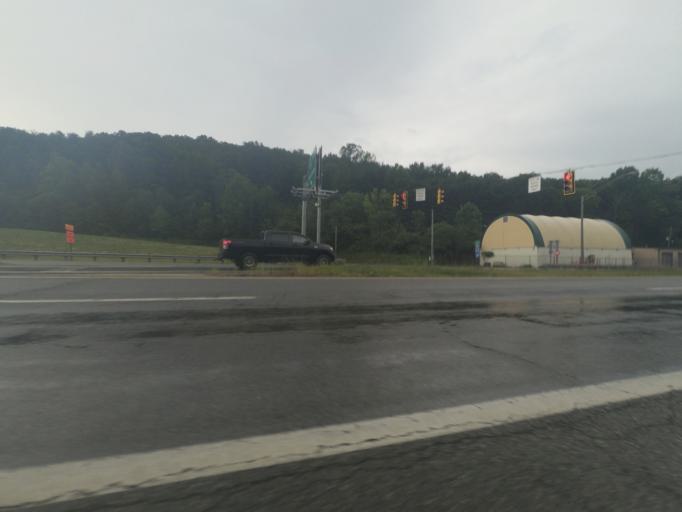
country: US
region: West Virginia
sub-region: Cabell County
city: Huntington
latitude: 38.3922
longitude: -82.4020
